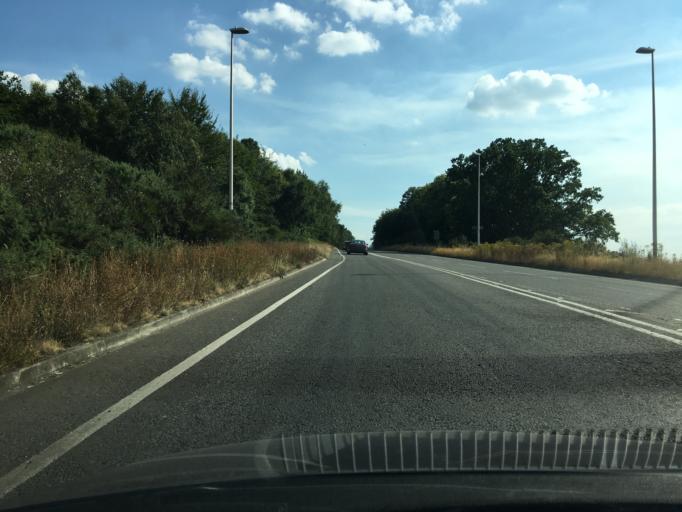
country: GB
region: England
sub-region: Bracknell Forest
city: Crowthorne
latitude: 51.3676
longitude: -0.7657
